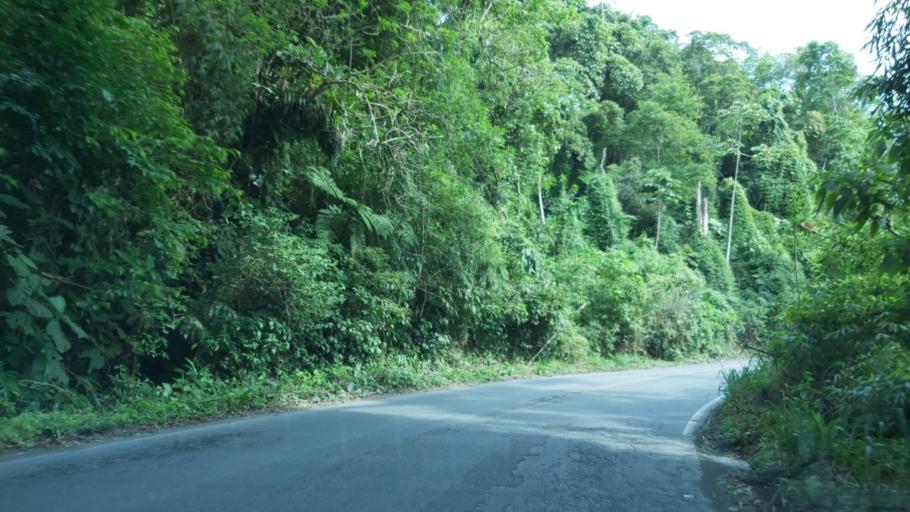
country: BR
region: Sao Paulo
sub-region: Juquia
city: Juquia
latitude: -24.0936
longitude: -47.6163
